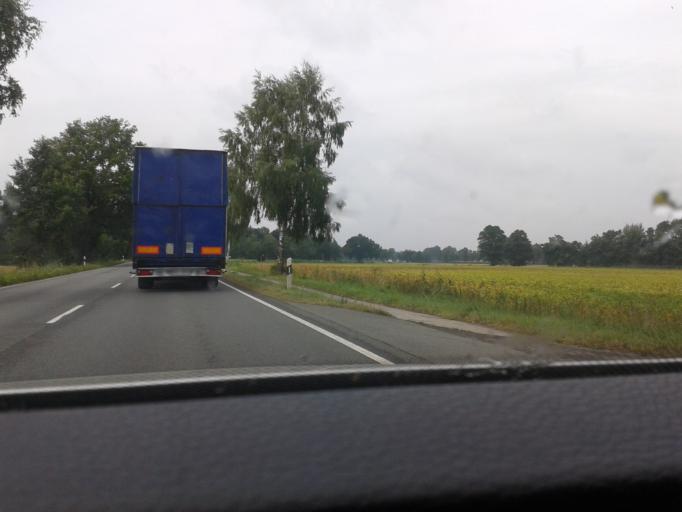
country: DE
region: Lower Saxony
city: Osloss
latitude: 52.4797
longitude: 10.6455
